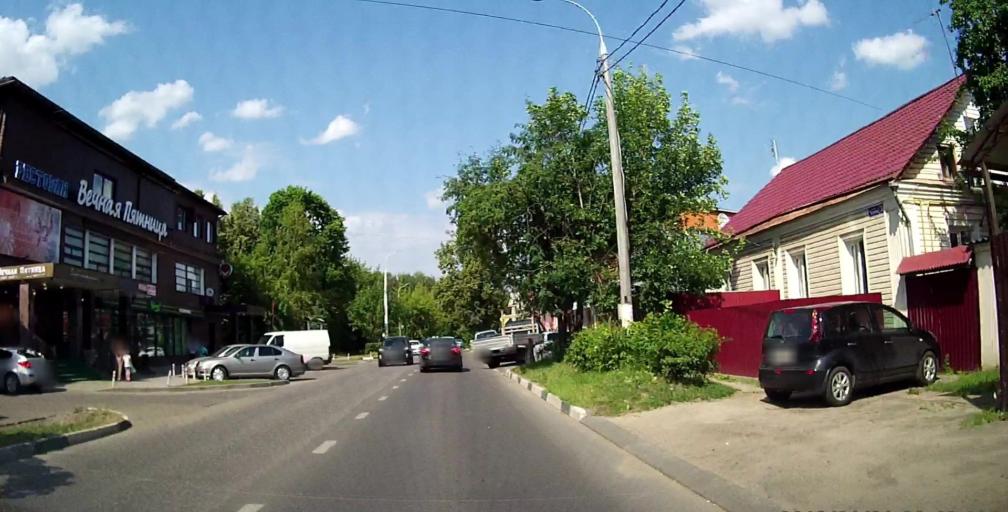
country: RU
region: Moskovskaya
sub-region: Podol'skiy Rayon
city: Podol'sk
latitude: 55.4132
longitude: 37.5265
